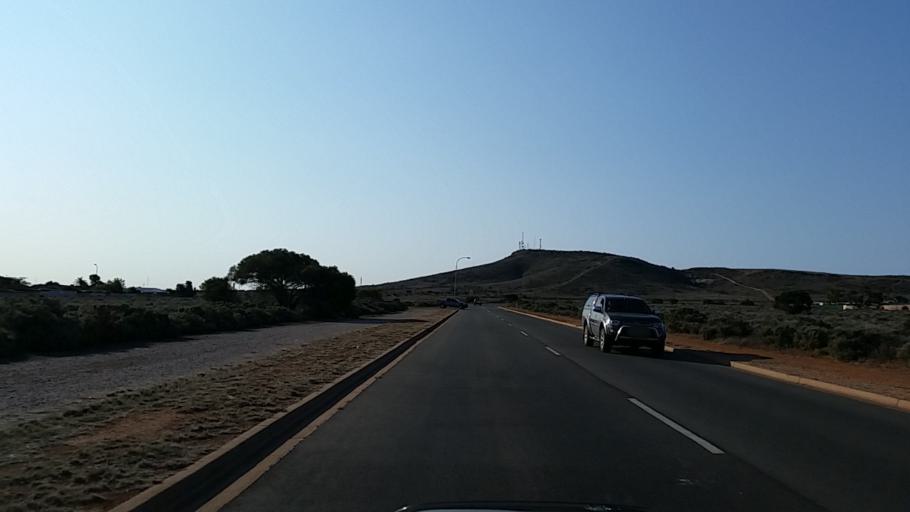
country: AU
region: South Australia
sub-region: Whyalla
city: Whyalla
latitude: -33.0130
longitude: 137.5287
